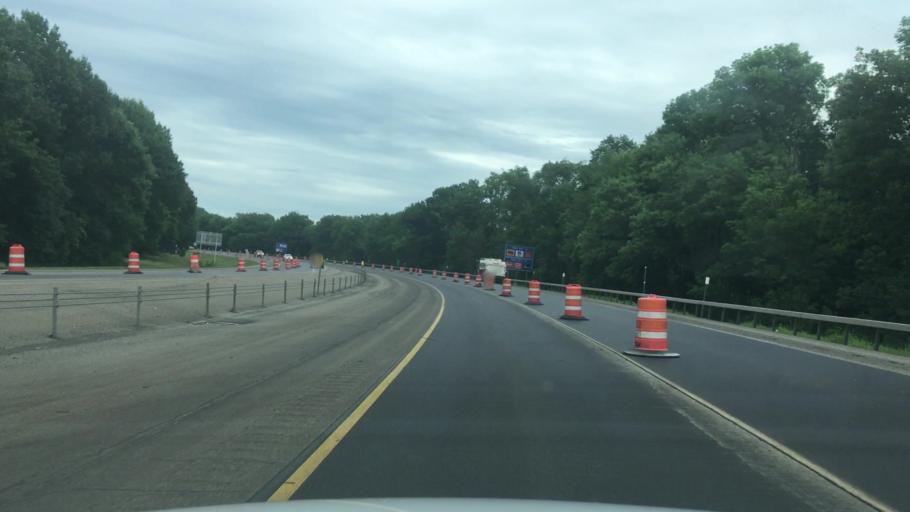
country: US
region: New York
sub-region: Otsego County
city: Oneonta
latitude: 42.4412
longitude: -75.0739
